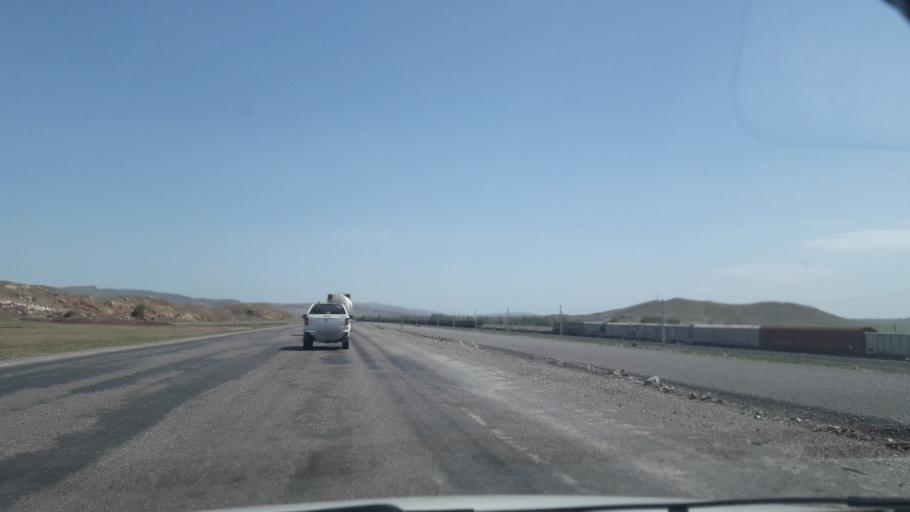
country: TR
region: Sivas
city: Ulas
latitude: 39.5364
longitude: 37.0191
